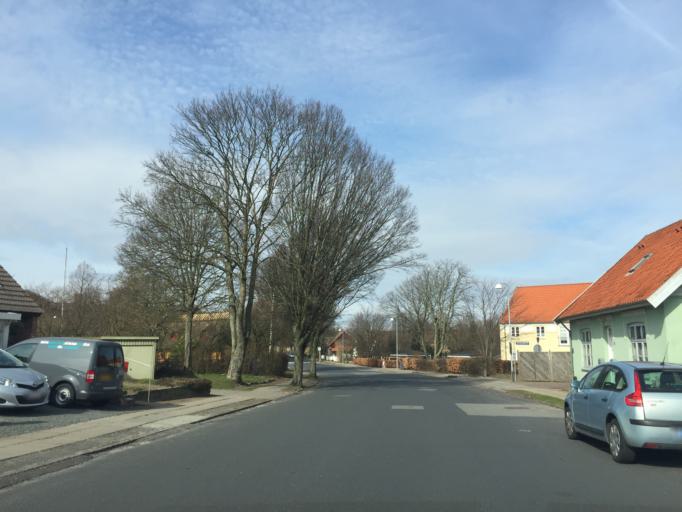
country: DK
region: South Denmark
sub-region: Odense Kommune
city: Seden
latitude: 55.3957
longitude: 10.4279
